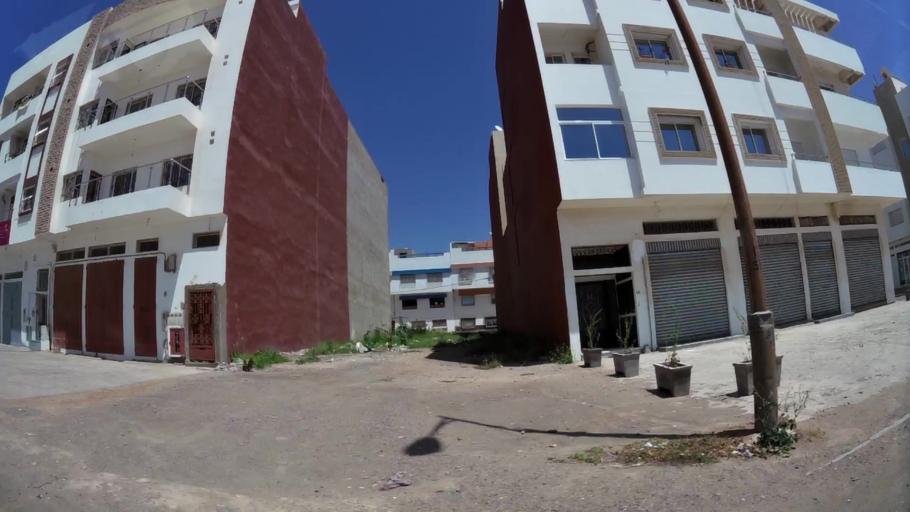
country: MA
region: Oued ed Dahab-Lagouira
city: Dakhla
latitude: 30.4284
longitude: -9.5601
